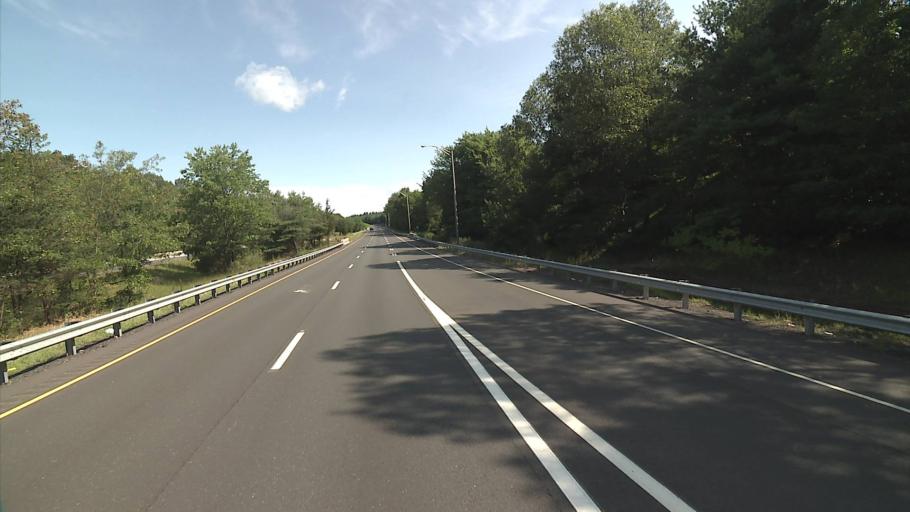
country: US
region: Connecticut
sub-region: Hartford County
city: Glastonbury Center
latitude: 41.6808
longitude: -72.5413
